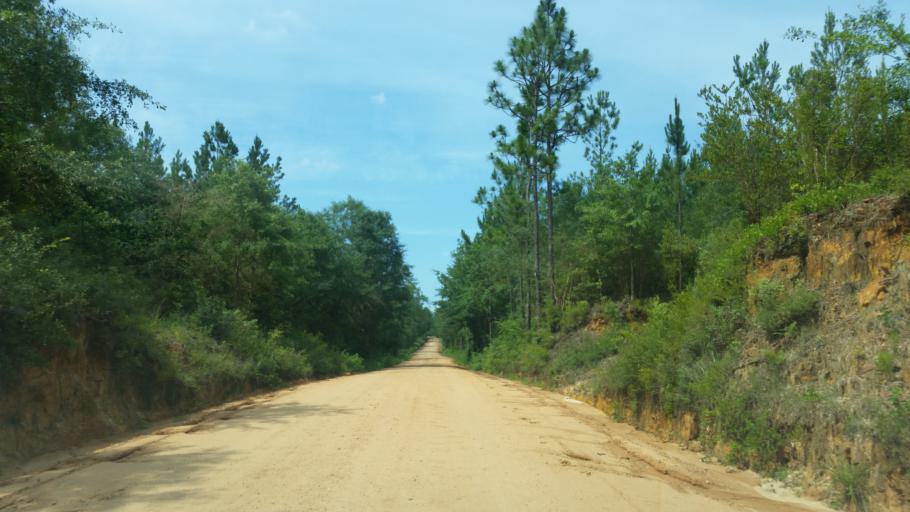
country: US
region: Florida
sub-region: Escambia County
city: Cantonment
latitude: 30.6199
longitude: -87.3859
